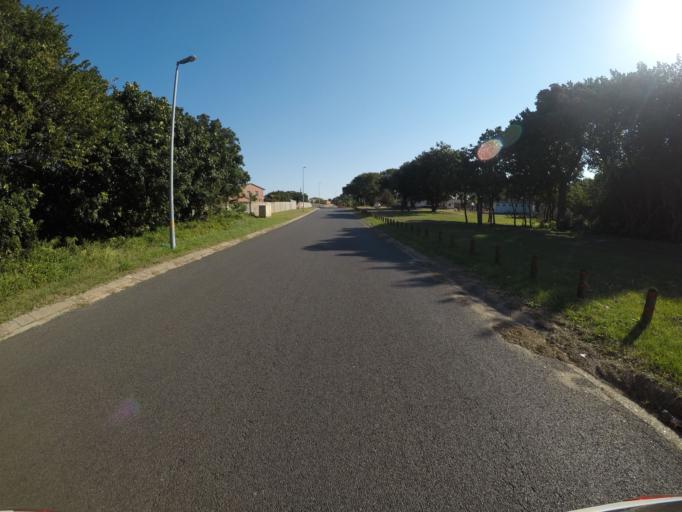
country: ZA
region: KwaZulu-Natal
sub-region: uThungulu District Municipality
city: Richards Bay
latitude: -28.7665
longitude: 32.0567
